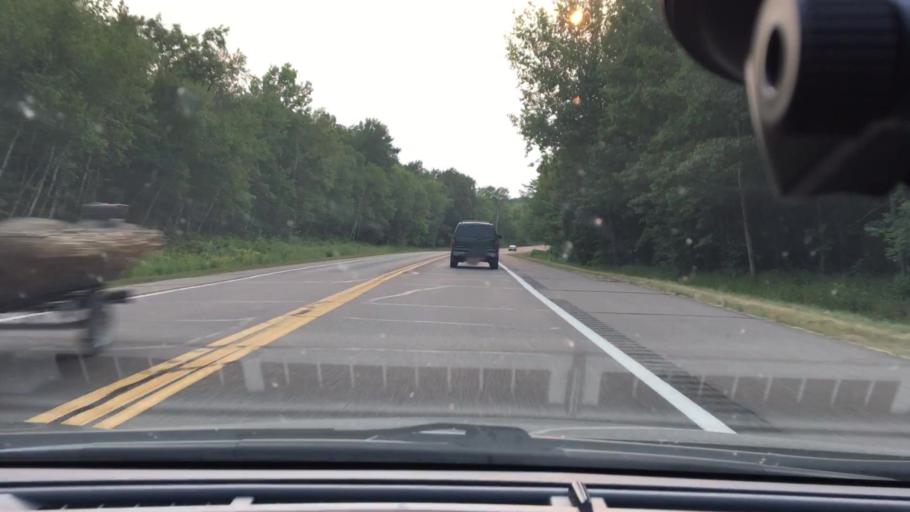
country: US
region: Minnesota
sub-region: Mille Lacs County
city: Vineland
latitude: 46.2028
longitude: -93.7758
